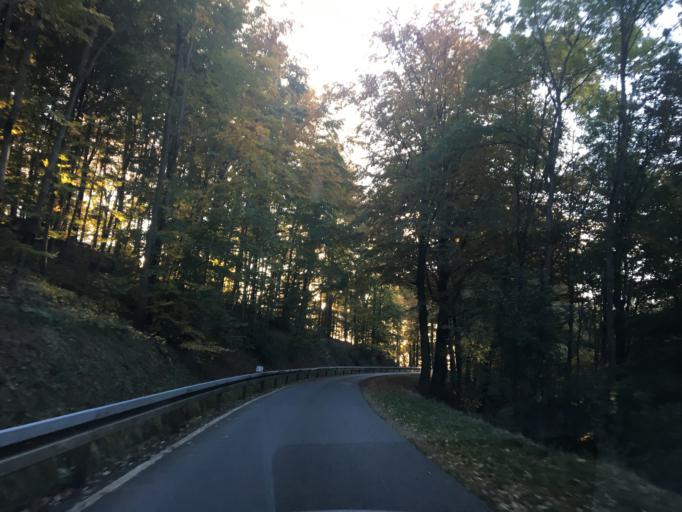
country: DE
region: Hesse
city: Zwingenberg
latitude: 49.7133
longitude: 8.6361
